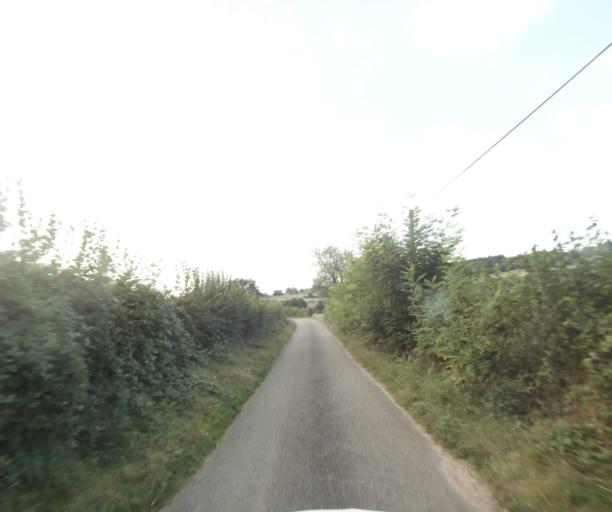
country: FR
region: Bourgogne
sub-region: Departement de Saone-et-Loire
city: Charolles
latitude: 46.4461
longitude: 4.3692
